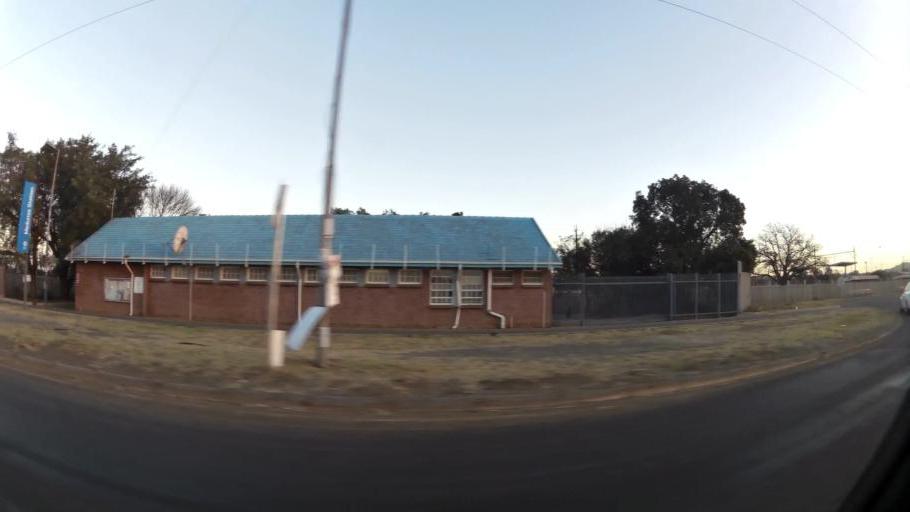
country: ZA
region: North-West
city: Ga-Rankuwa
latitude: -25.6214
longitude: 28.0189
